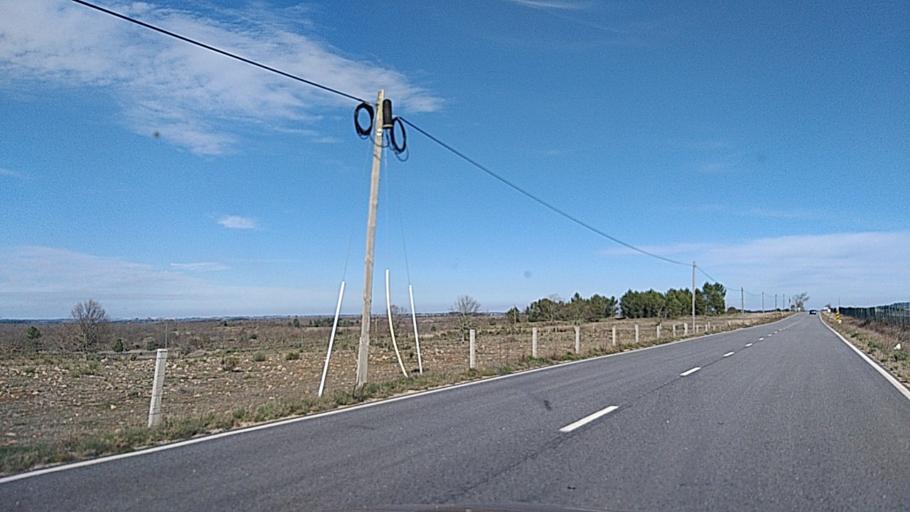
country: ES
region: Castille and Leon
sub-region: Provincia de Salamanca
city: Fuentes de Onoro
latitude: 40.5933
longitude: -6.9849
